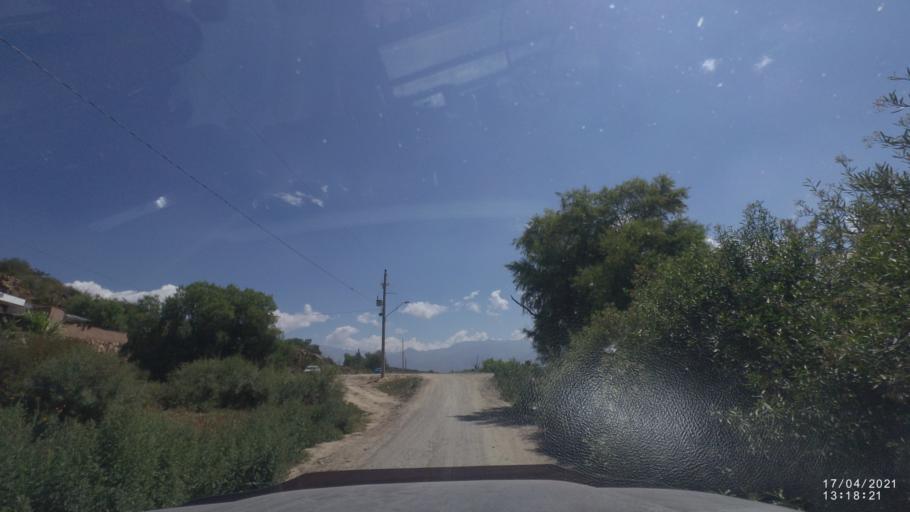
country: BO
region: Cochabamba
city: Cochabamba
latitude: -17.4154
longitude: -66.2429
